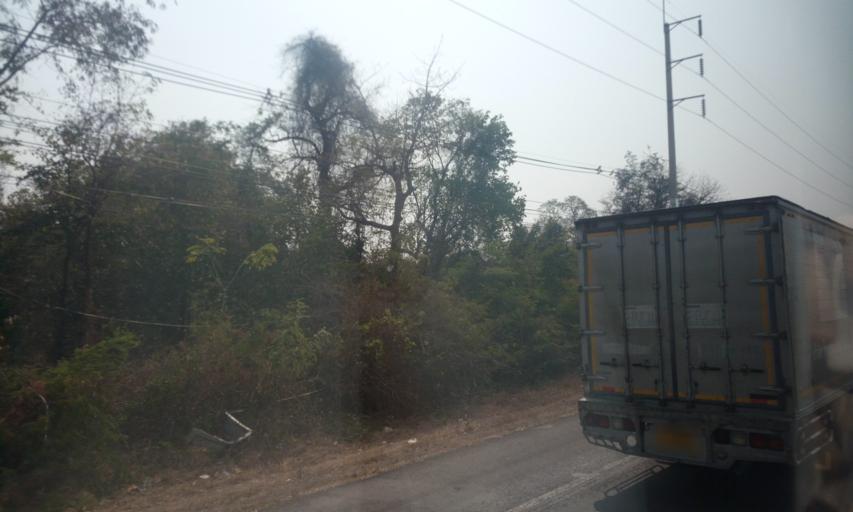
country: TH
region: Nakhon Ratchasima
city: Sida
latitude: 15.5853
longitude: 102.5574
